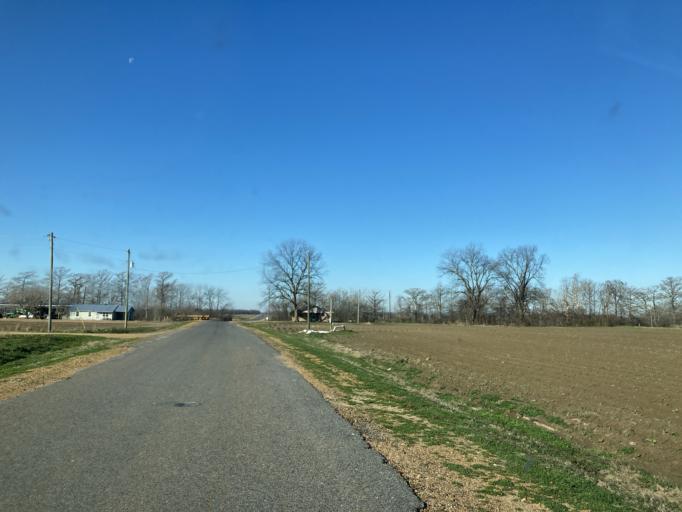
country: US
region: Mississippi
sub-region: Yazoo County
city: Yazoo City
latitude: 32.9519
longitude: -90.5898
